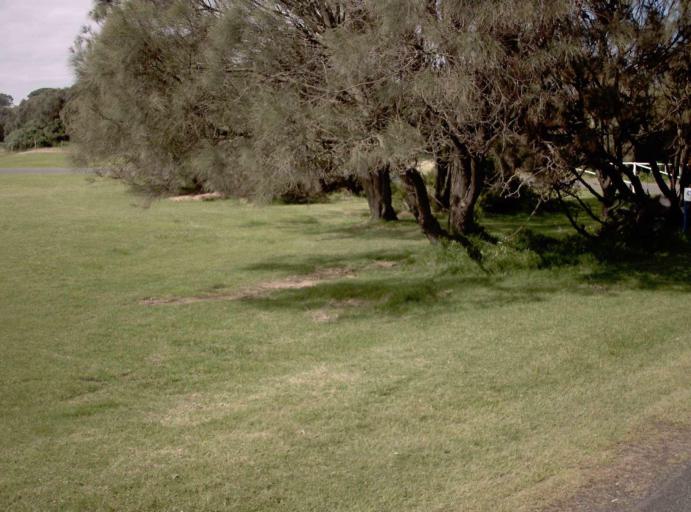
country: AU
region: Victoria
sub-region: Bass Coast
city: Phillip Island
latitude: -38.5062
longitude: 145.1461
